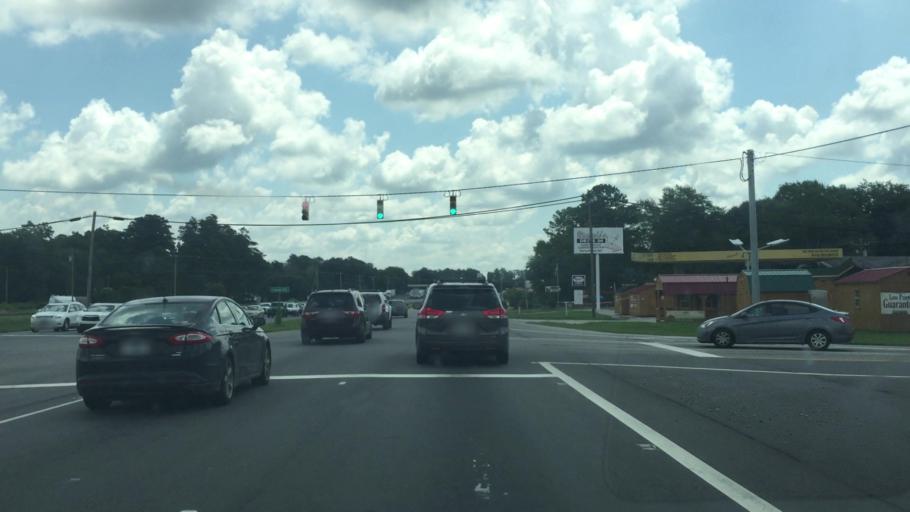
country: US
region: North Carolina
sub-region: Scotland County
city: Laurel Hill
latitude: 34.8087
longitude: -79.5486
